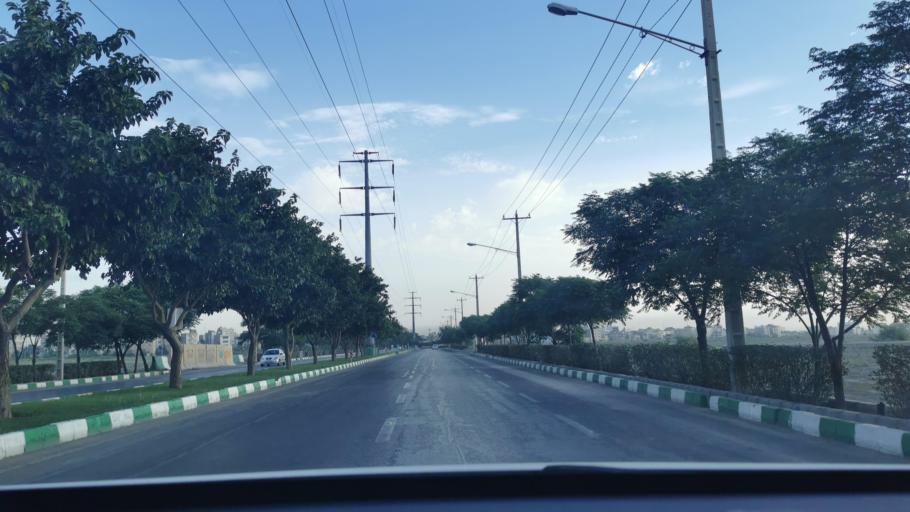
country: IR
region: Razavi Khorasan
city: Mashhad
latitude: 36.3459
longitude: 59.5313
